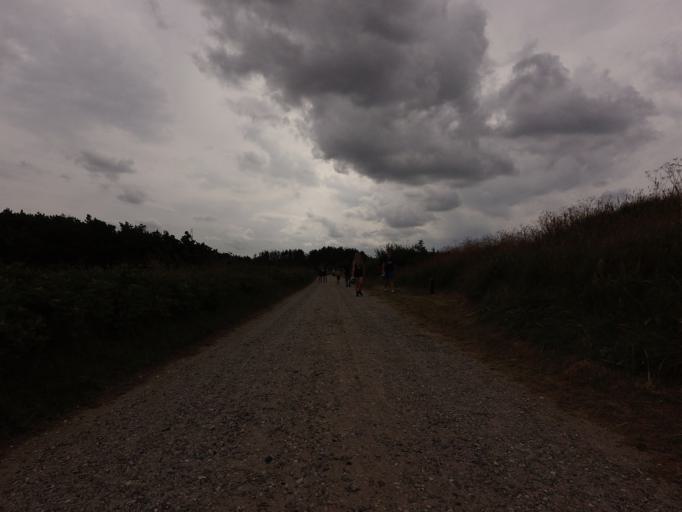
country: DK
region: North Denmark
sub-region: Jammerbugt Kommune
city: Pandrup
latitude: 57.3278
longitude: 9.6731
